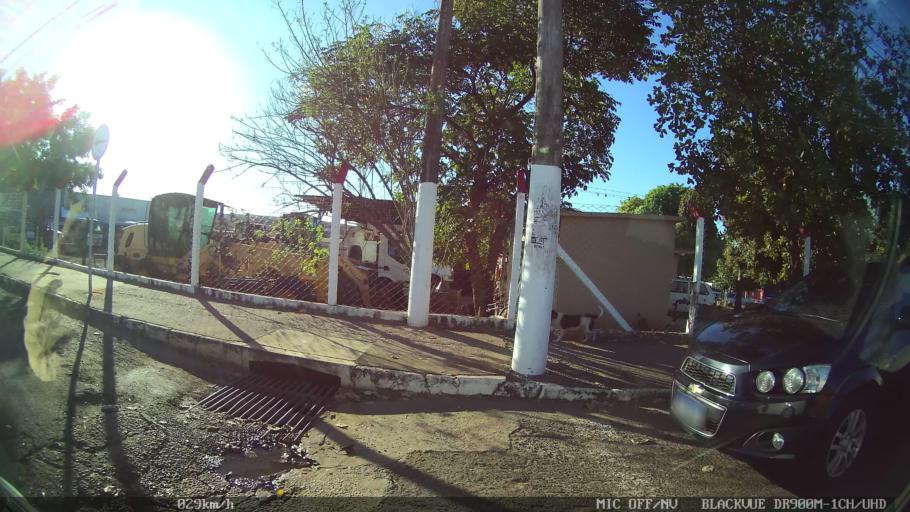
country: BR
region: Sao Paulo
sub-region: Guapiacu
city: Guapiacu
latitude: -20.7945
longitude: -49.2265
